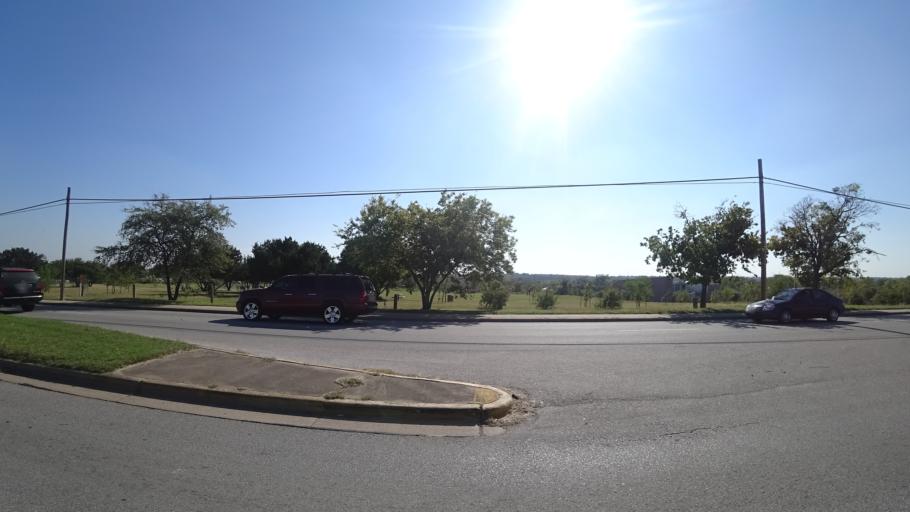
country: US
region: Texas
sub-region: Travis County
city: Wells Branch
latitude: 30.3534
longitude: -97.6801
